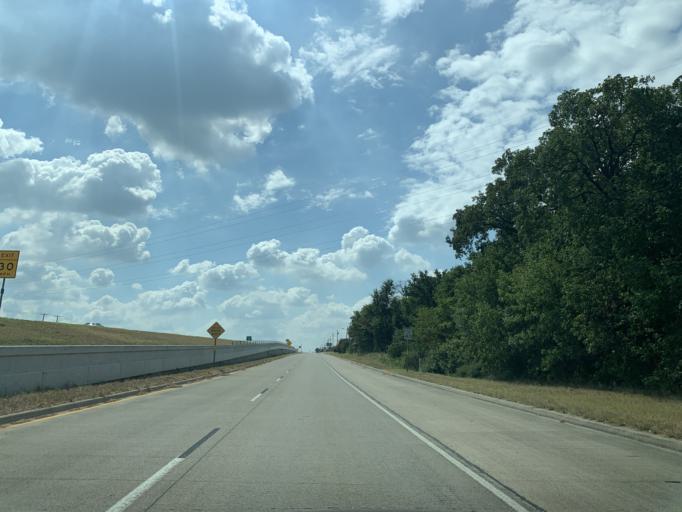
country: US
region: Texas
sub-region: Tarrant County
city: Lakeside
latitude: 32.8311
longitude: -97.4852
